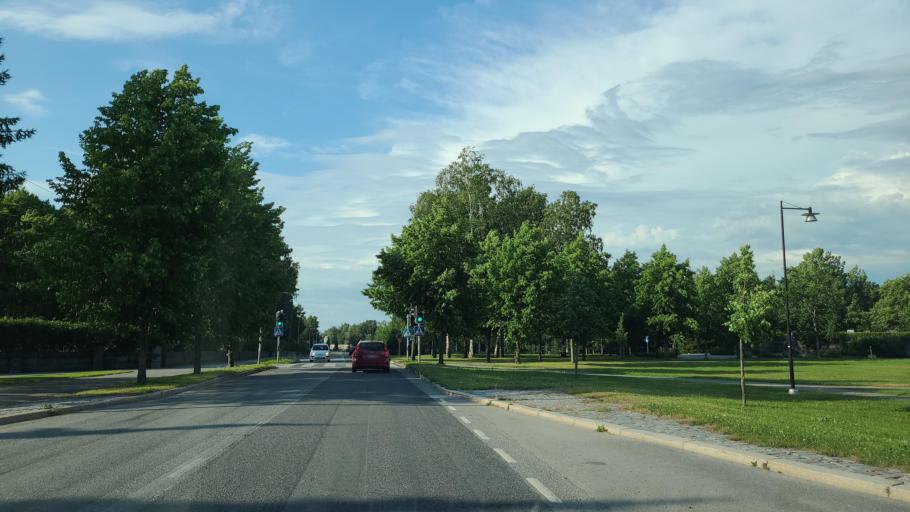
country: FI
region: Ostrobothnia
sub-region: Vaasa
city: Vaasa
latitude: 63.1072
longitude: 21.6181
